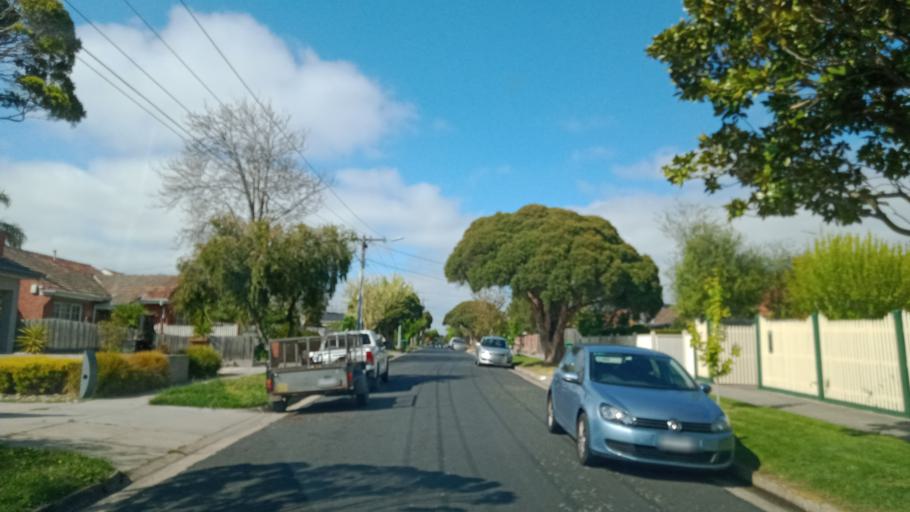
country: AU
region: Victoria
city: Hughesdale
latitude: -37.9130
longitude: 145.0794
